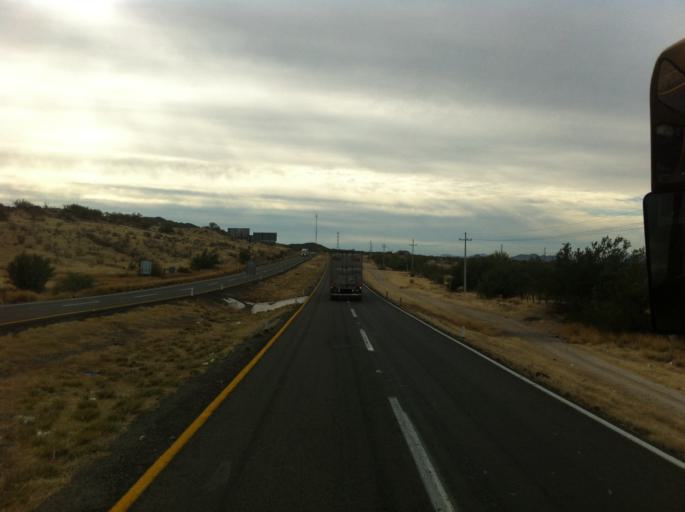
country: MX
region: Sonora
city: Hermosillo
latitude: 28.9842
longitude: -110.9681
